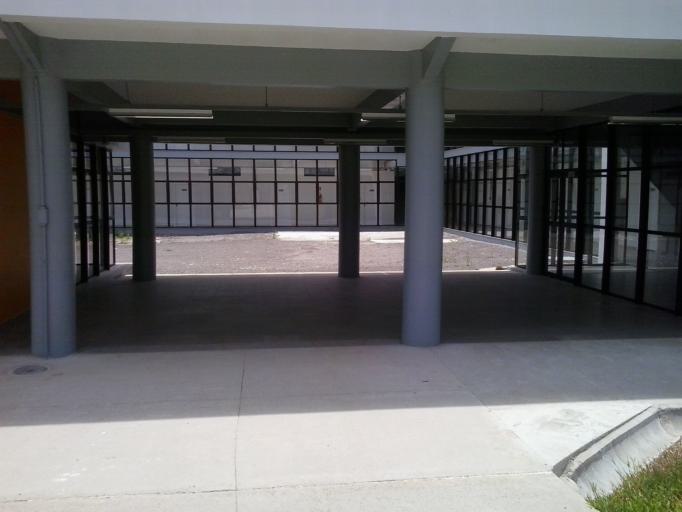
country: BR
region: Rio Grande do Sul
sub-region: Santa Maria
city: Santa Maria
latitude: -29.7197
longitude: -53.7195
